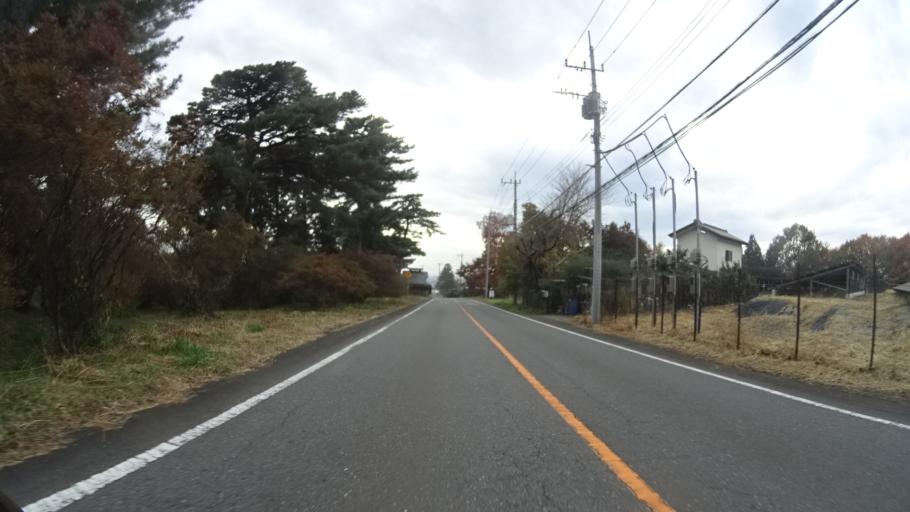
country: JP
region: Gunma
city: Omamacho-omama
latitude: 36.4624
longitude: 139.1748
